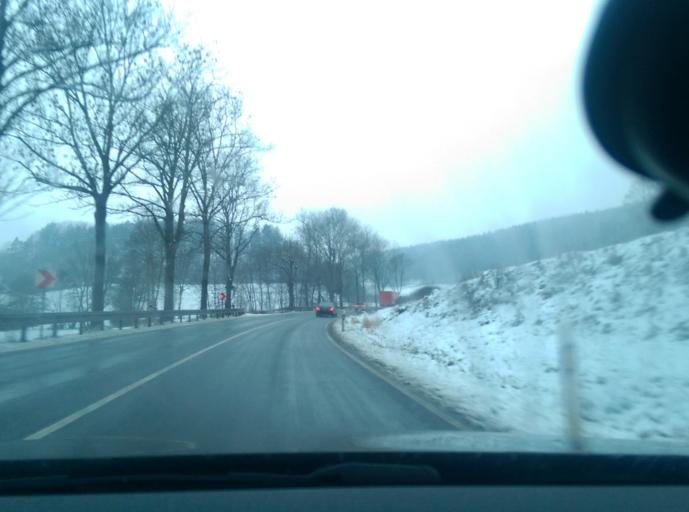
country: DE
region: Hesse
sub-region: Regierungsbezirk Kassel
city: Grossalmerode
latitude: 51.1810
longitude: 9.8011
